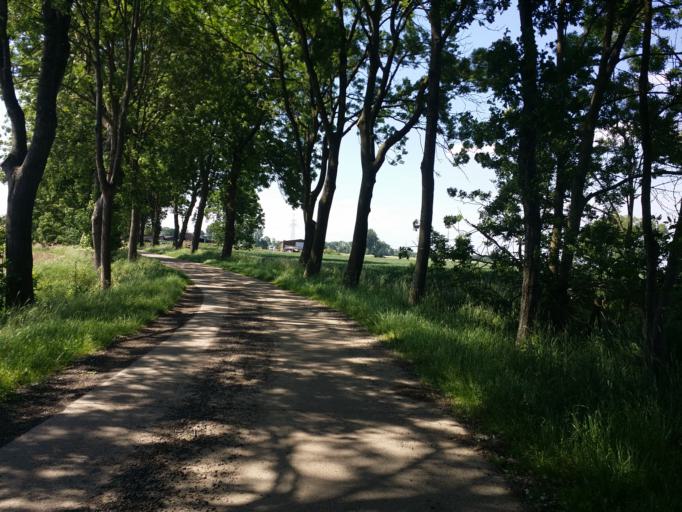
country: DE
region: Lower Saxony
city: Neuenkirchen
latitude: 53.1609
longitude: 8.5243
